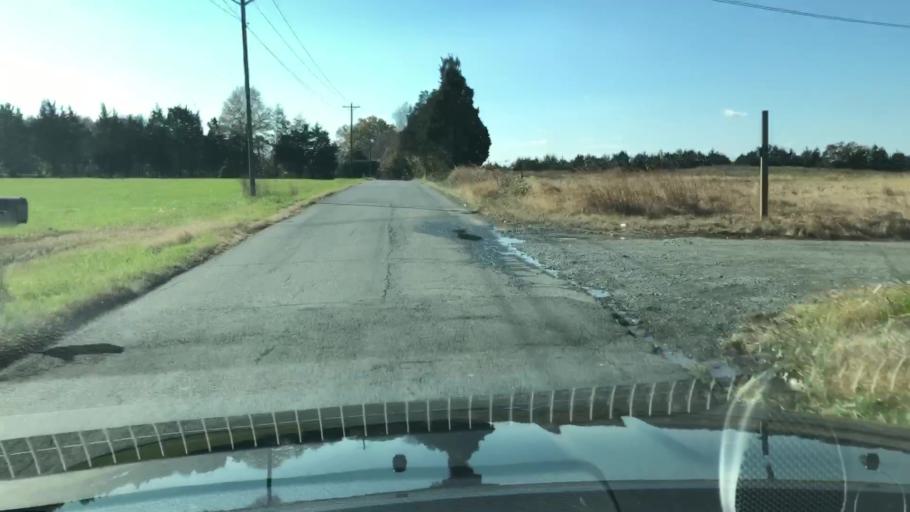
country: US
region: Virginia
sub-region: Fauquier County
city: Bealeton
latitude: 38.5173
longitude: -77.7483
